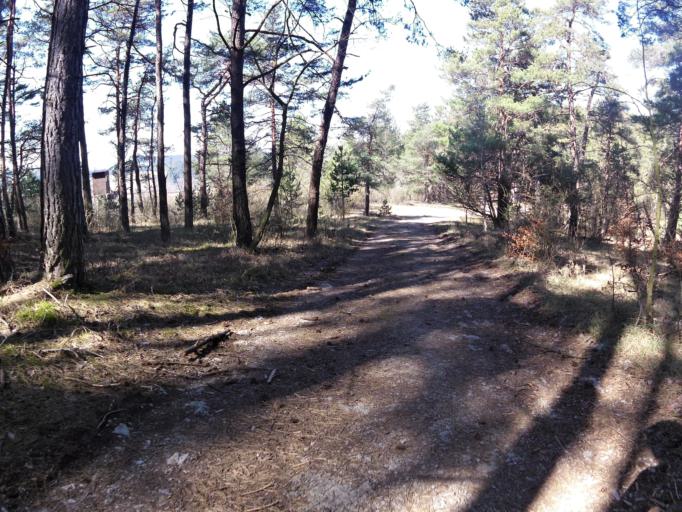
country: DE
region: Bavaria
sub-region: Regierungsbezirk Unterfranken
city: Erlabrunn
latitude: 49.8493
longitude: 9.8138
